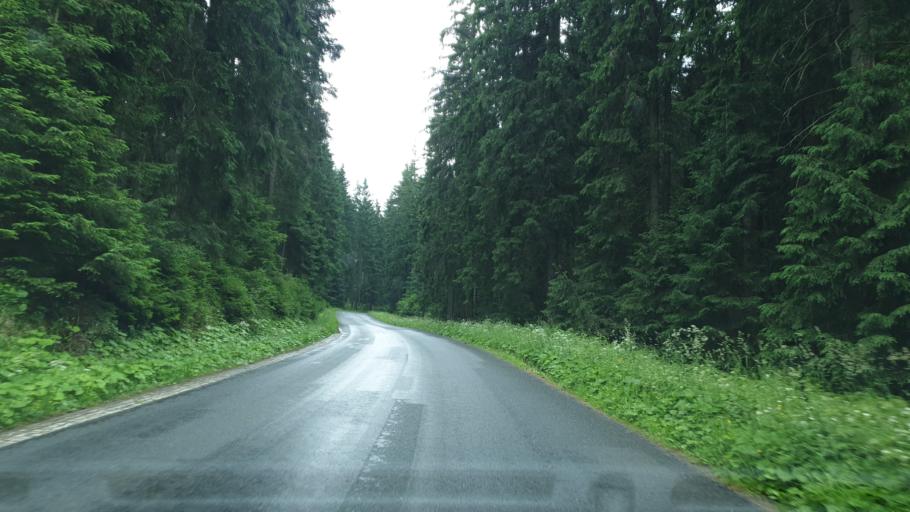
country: DE
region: Saxony
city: Tannenbergsthal
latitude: 50.4205
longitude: 12.4492
